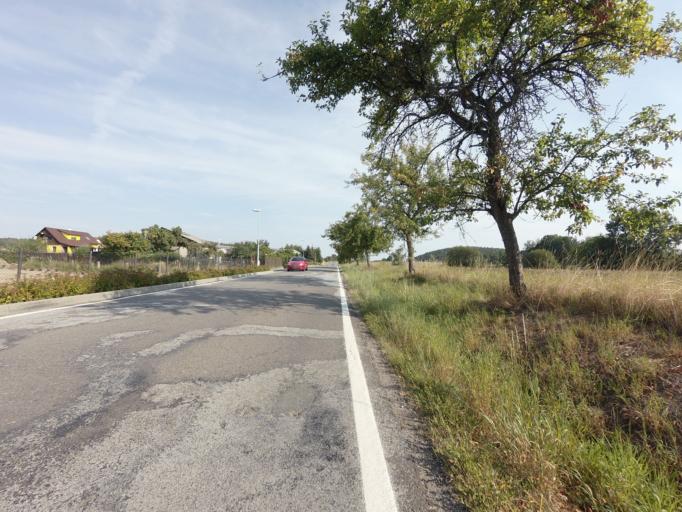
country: CZ
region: Jihocesky
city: Milevsko
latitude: 49.4621
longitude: 14.3629
